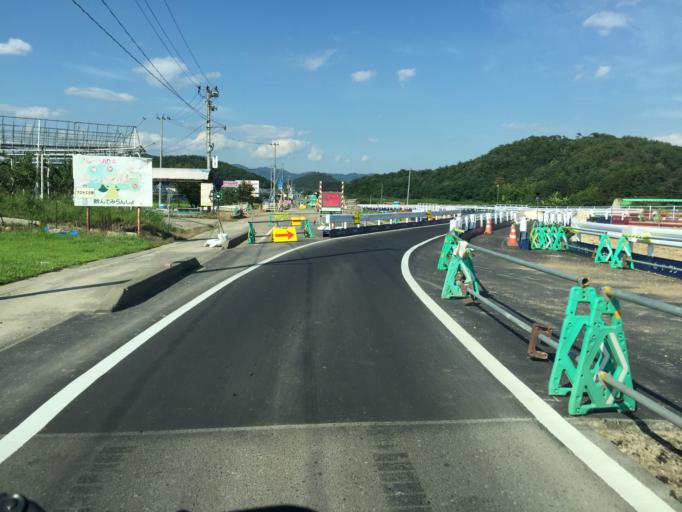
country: JP
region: Fukushima
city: Fukushima-shi
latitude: 37.8061
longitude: 140.4115
